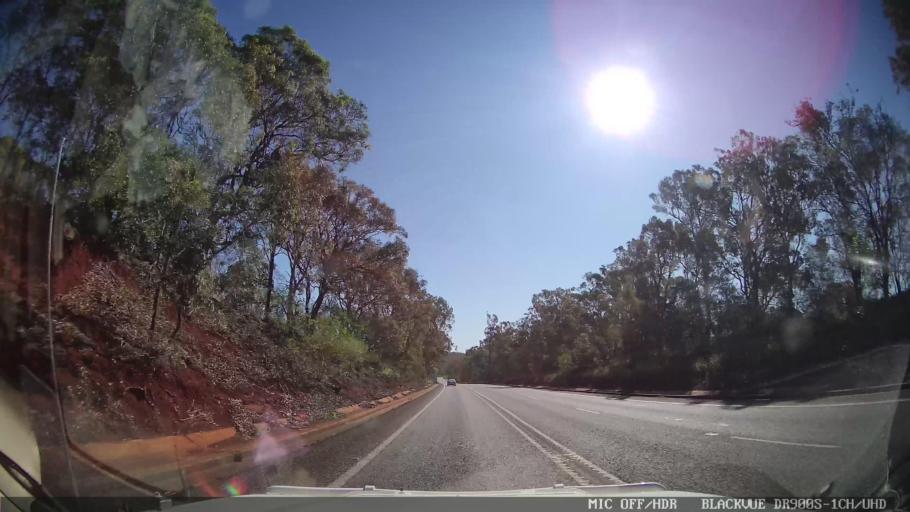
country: AU
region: Queensland
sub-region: Bundaberg
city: Childers
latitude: -25.2347
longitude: 152.2491
